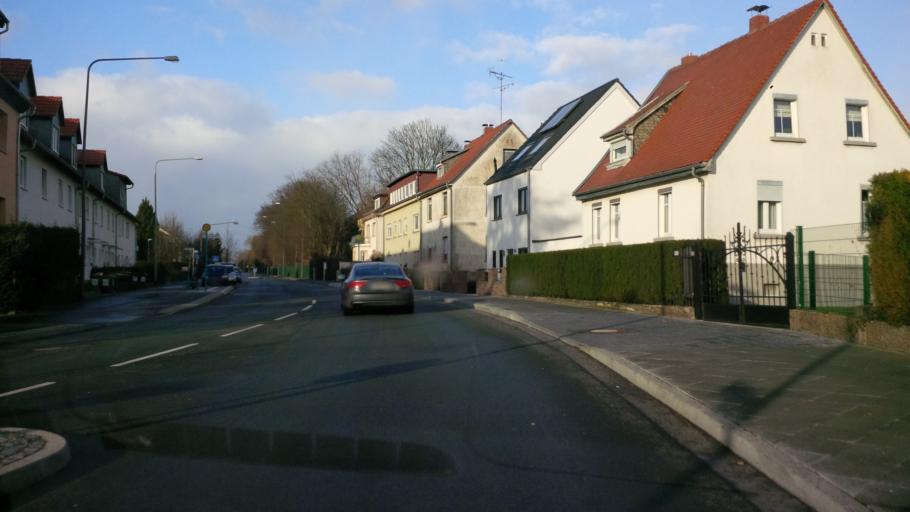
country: DE
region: Hesse
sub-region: Regierungsbezirk Darmstadt
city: Bad Homburg vor der Hoehe
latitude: 50.1969
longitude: 8.6666
